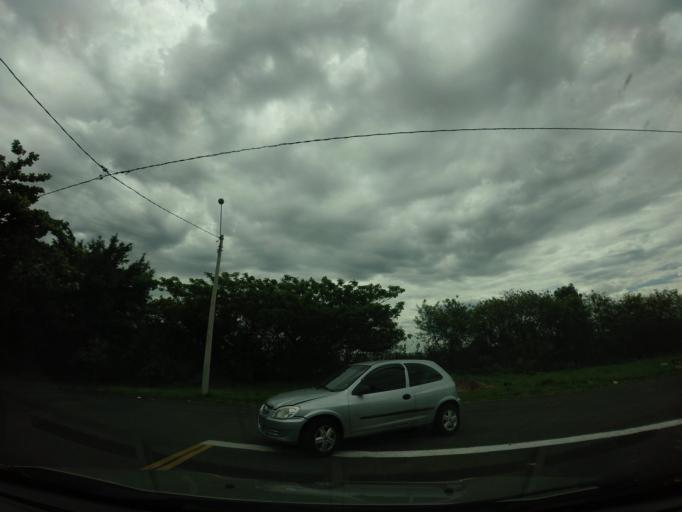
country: BR
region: Sao Paulo
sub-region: Piracicaba
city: Piracicaba
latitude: -22.7585
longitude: -47.6025
